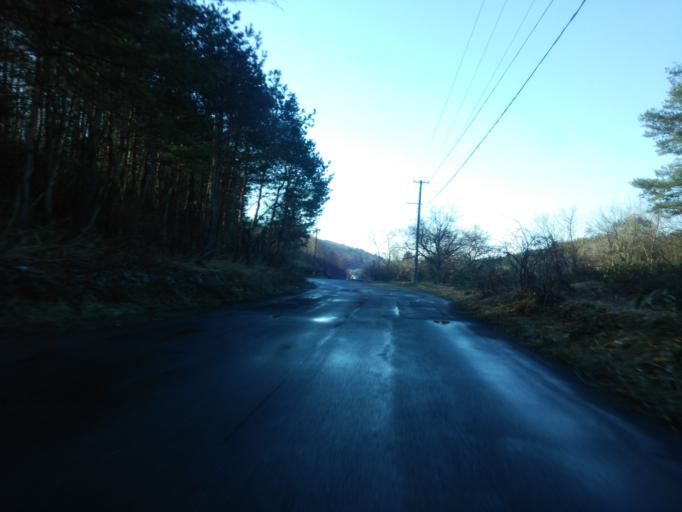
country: JP
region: Fukushima
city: Kitakata
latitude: 37.7008
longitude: 139.7870
